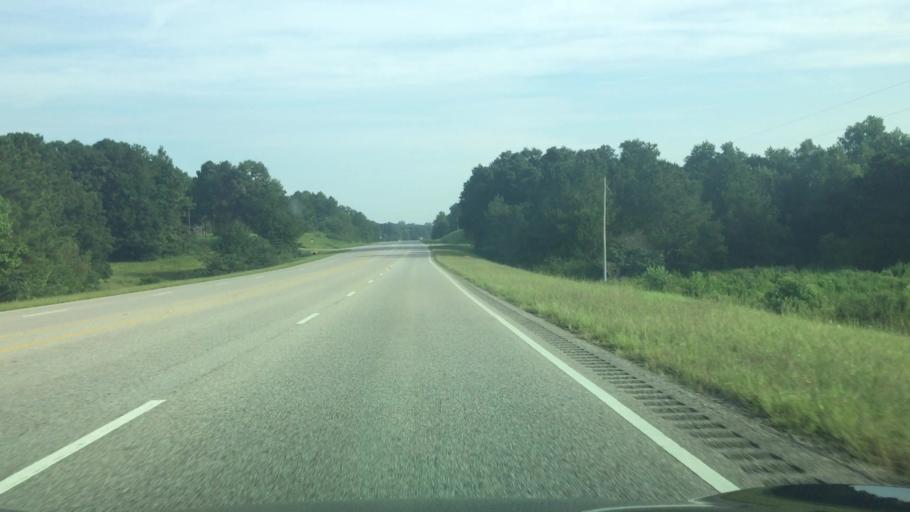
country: US
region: Alabama
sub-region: Covington County
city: Andalusia
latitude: 31.4134
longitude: -86.6069
